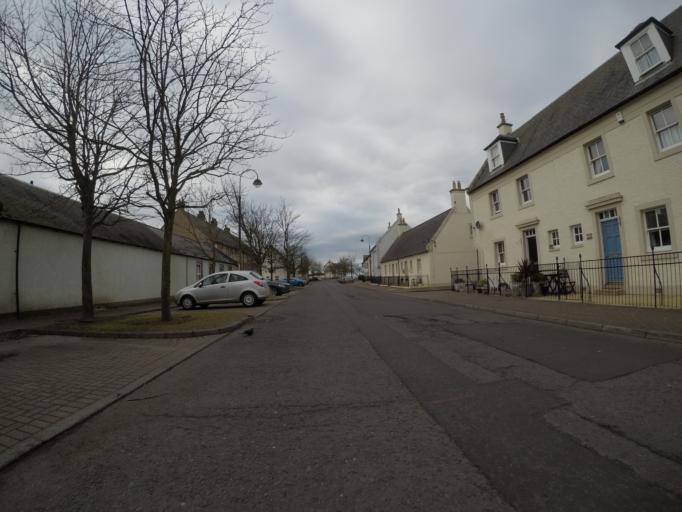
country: GB
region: Scotland
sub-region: North Ayrshire
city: Irvine
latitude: 55.6088
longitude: -4.6792
